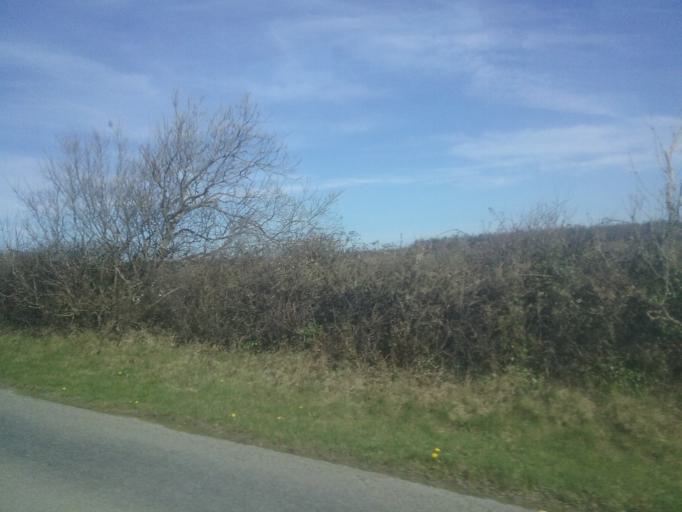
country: IE
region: Munster
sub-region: An Clar
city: Kilrush
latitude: 52.6169
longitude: -9.4564
